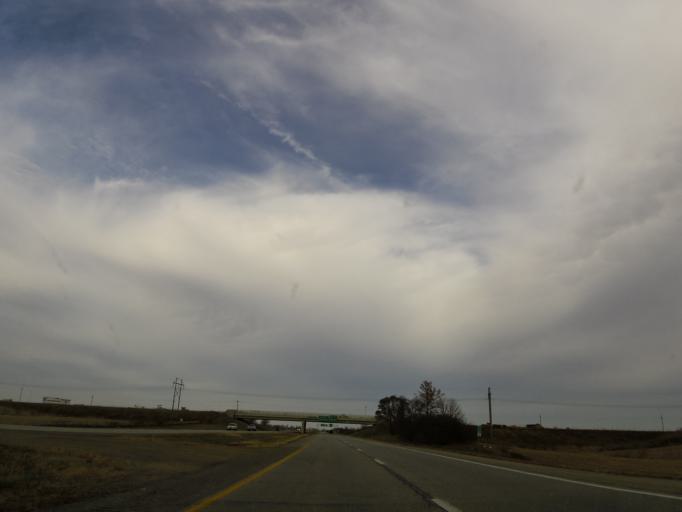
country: US
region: Iowa
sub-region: Scott County
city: Bettendorf
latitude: 41.5874
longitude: -90.5221
